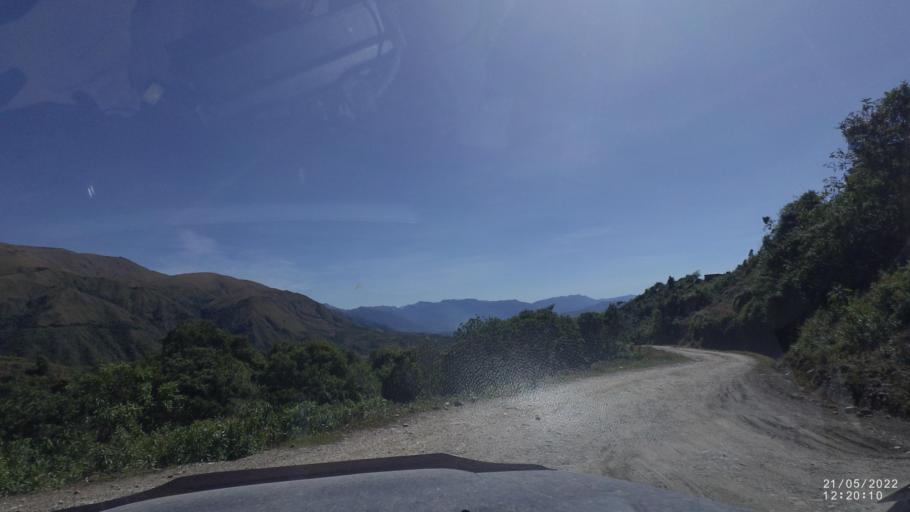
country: BO
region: Cochabamba
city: Colomi
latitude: -17.2257
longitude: -65.9034
